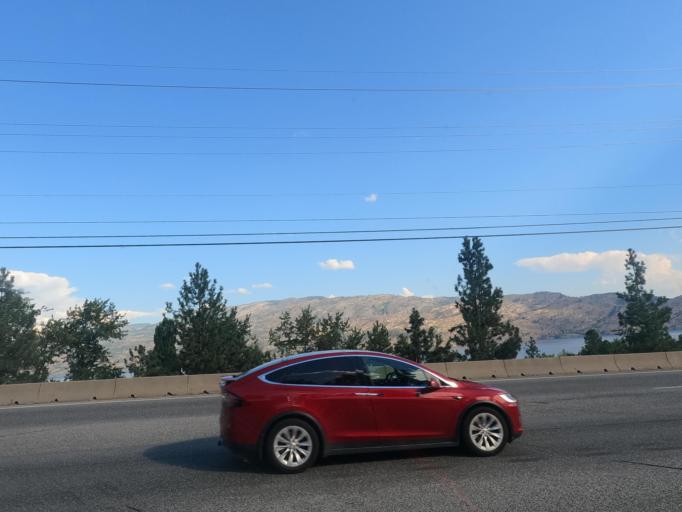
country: CA
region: British Columbia
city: Peachland
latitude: 49.7861
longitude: -119.7107
